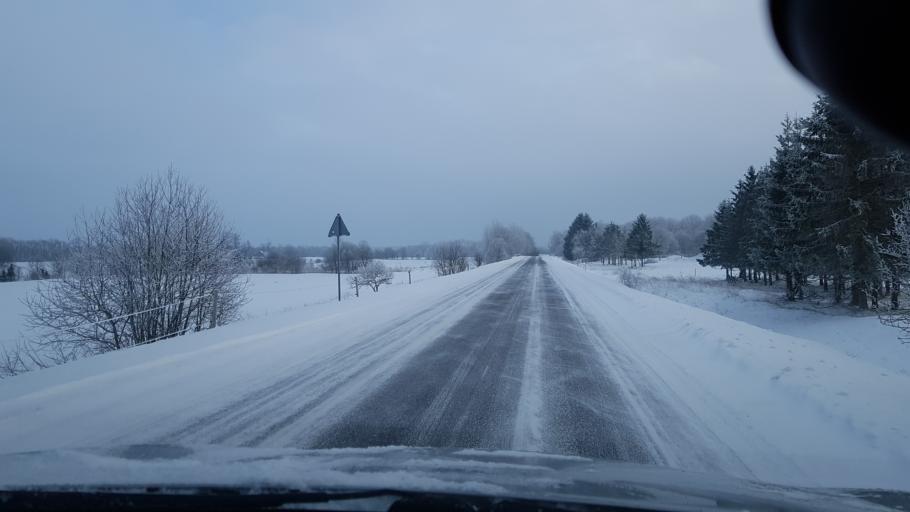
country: EE
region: Harju
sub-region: Keila linn
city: Keila
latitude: 59.3384
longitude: 24.4527
